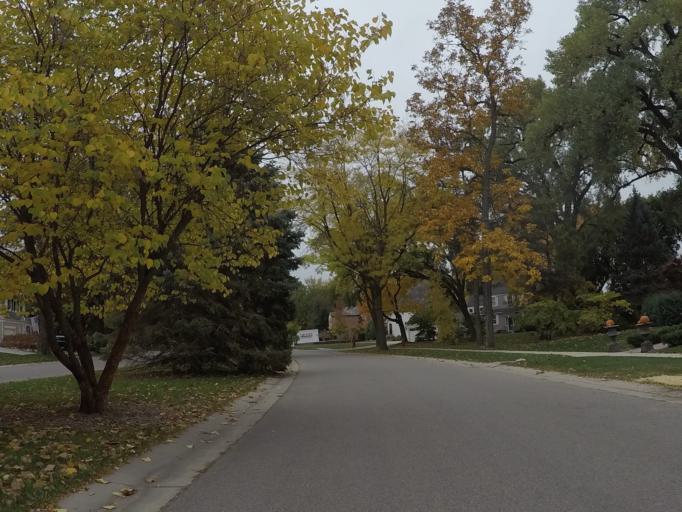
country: US
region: Wisconsin
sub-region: Dane County
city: Maple Bluff
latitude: 43.1061
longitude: -89.3670
